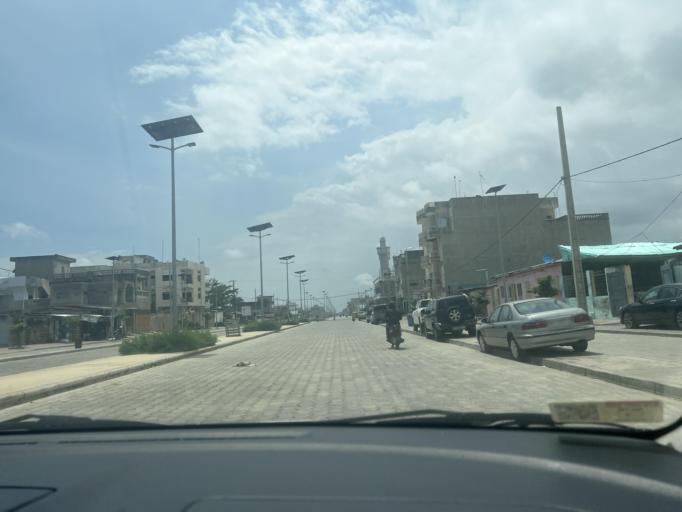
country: BJ
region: Littoral
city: Cotonou
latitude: 6.3886
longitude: 2.4483
